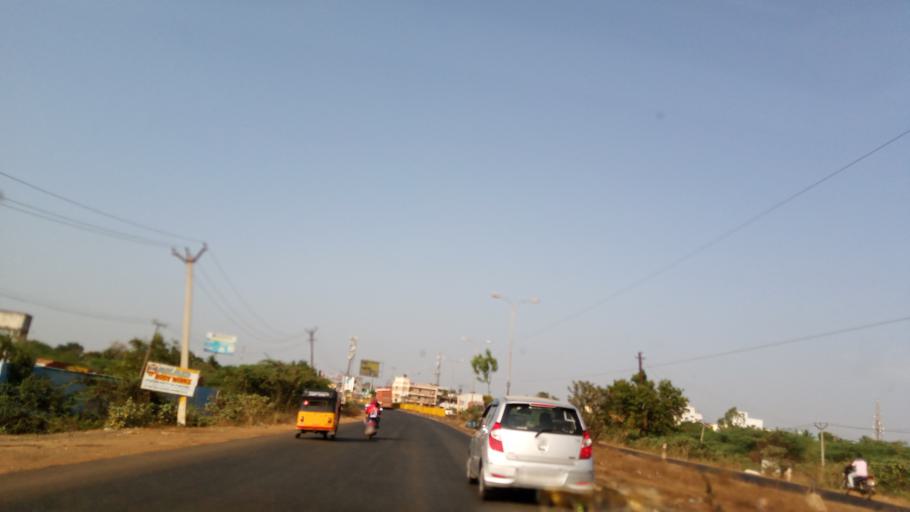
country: IN
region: Tamil Nadu
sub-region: Kancheepuram
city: Sriperumbudur
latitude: 12.9928
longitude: 79.9863
